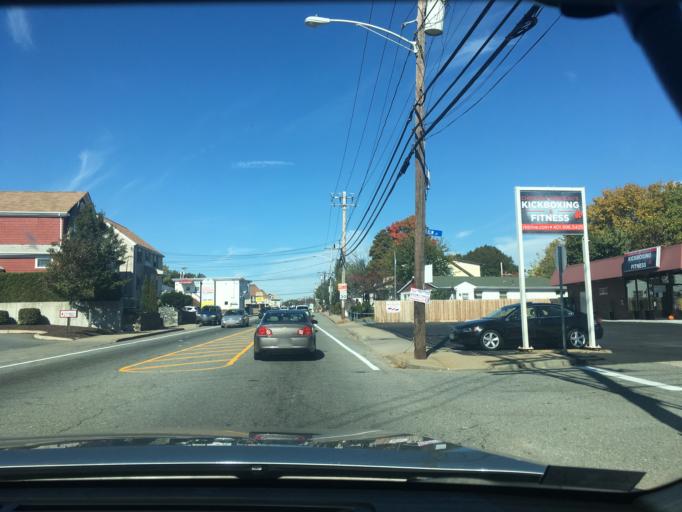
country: US
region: Rhode Island
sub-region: Providence County
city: North Providence
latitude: 41.8273
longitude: -71.4723
